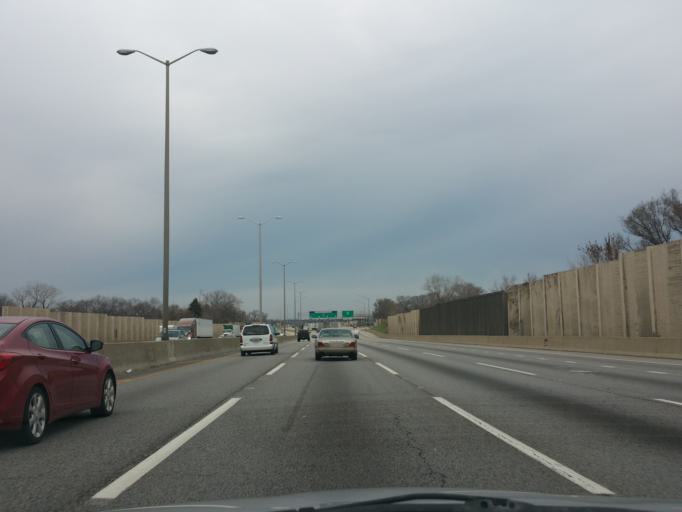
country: US
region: Illinois
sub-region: Cook County
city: Hickory Hills
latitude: 41.7355
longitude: -87.8211
